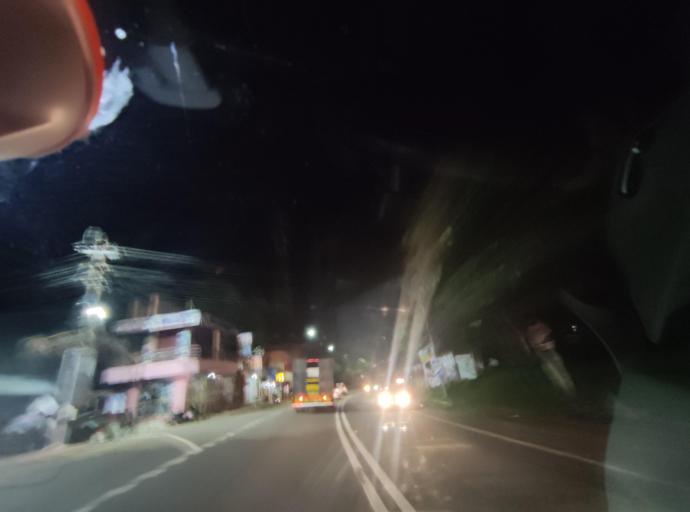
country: IN
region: Kerala
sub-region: Thiruvananthapuram
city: Attingal
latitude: 8.7427
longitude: 76.8974
